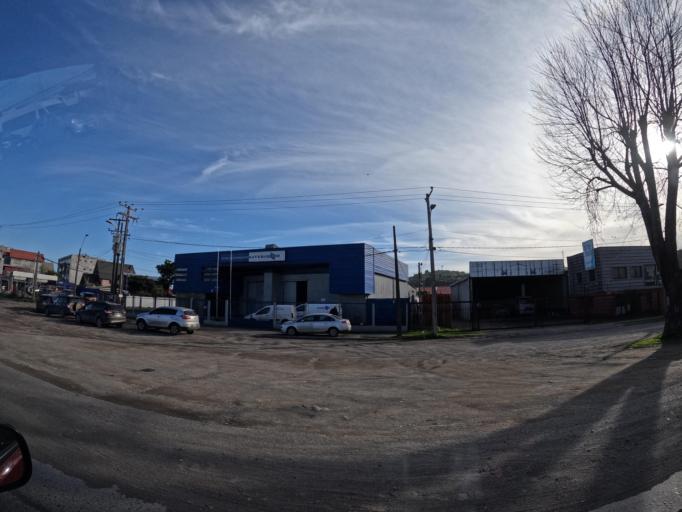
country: CL
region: Biobio
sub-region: Provincia de Concepcion
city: Talcahuano
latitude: -36.7689
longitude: -73.0842
